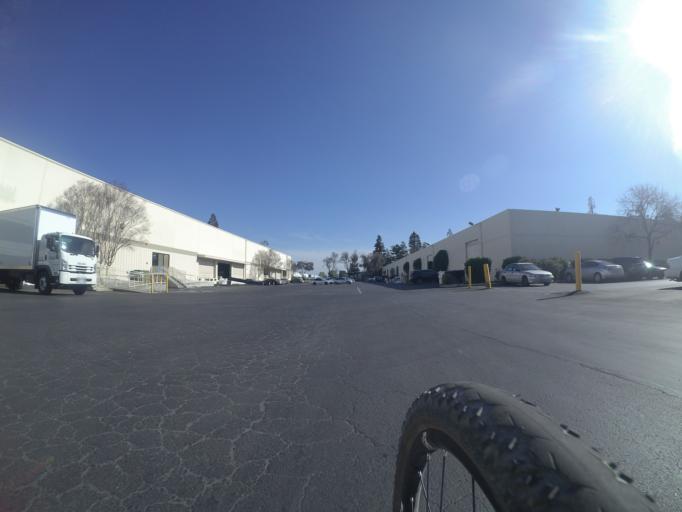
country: US
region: California
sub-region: Santa Clara County
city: Milpitas
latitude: 37.3826
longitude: -121.9171
